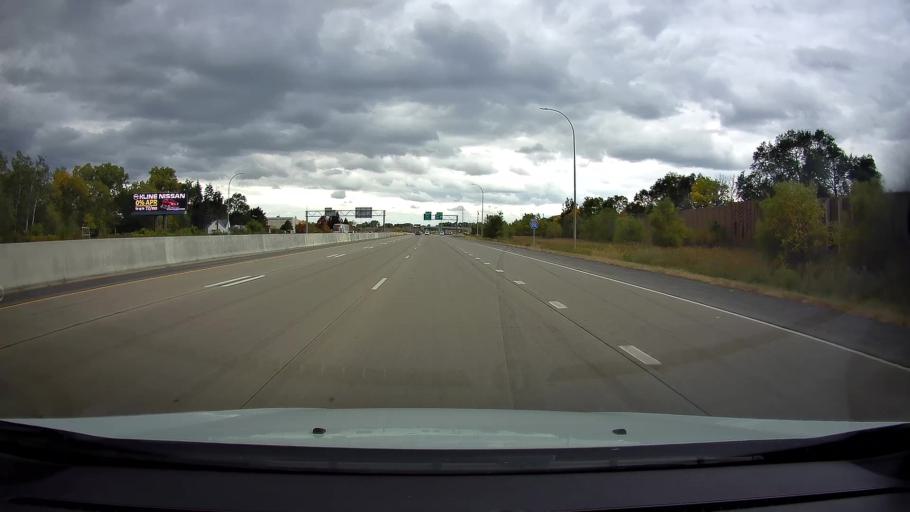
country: US
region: Minnesota
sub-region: Ramsey County
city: Vadnais Heights
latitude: 45.0449
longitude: -93.0613
